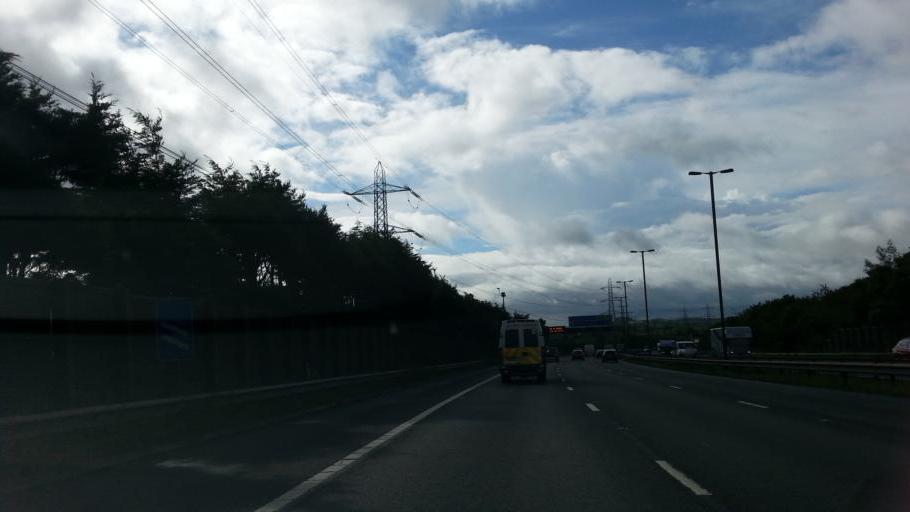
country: GB
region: England
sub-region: City and Borough of Birmingham
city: Bartley Green
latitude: 52.4570
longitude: -2.0120
